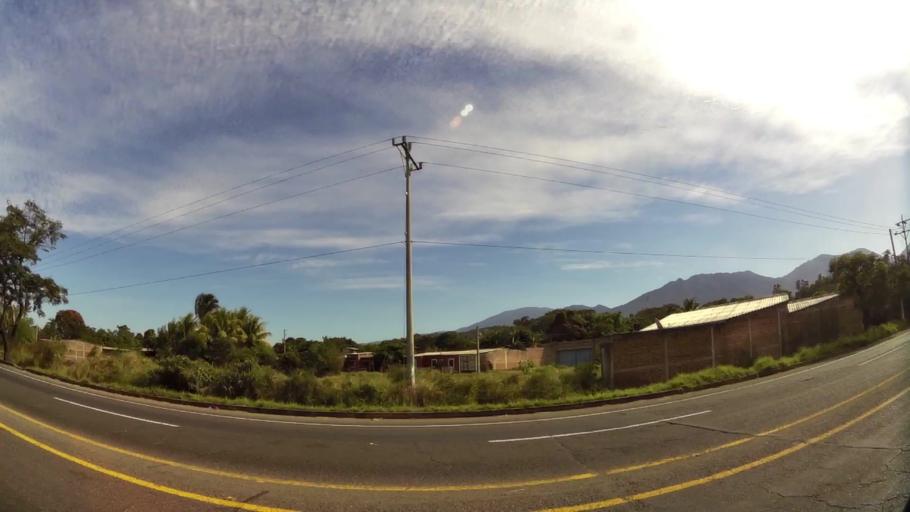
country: SV
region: Santa Ana
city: Chalchuapa
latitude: 13.9879
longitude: -89.6900
